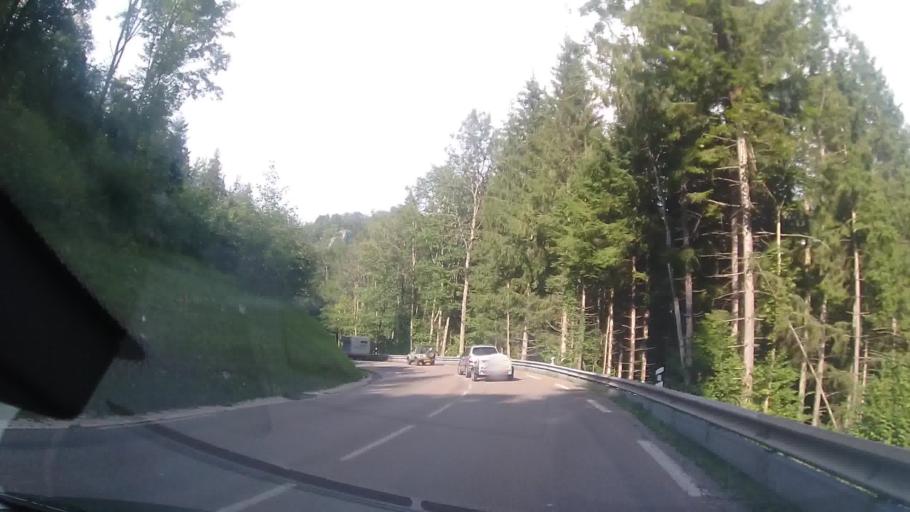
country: FR
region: Franche-Comte
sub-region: Departement du Jura
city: Champagnole
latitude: 46.6093
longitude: 5.8972
